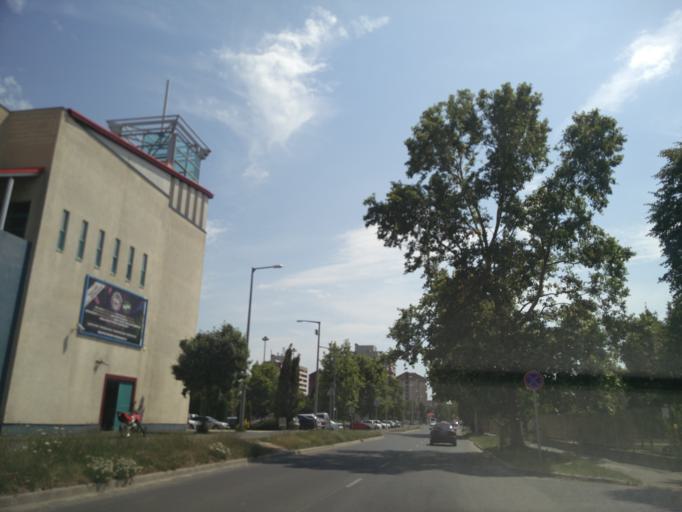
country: HU
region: Zala
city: Zalaegerszeg
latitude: 46.8476
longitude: 16.8510
